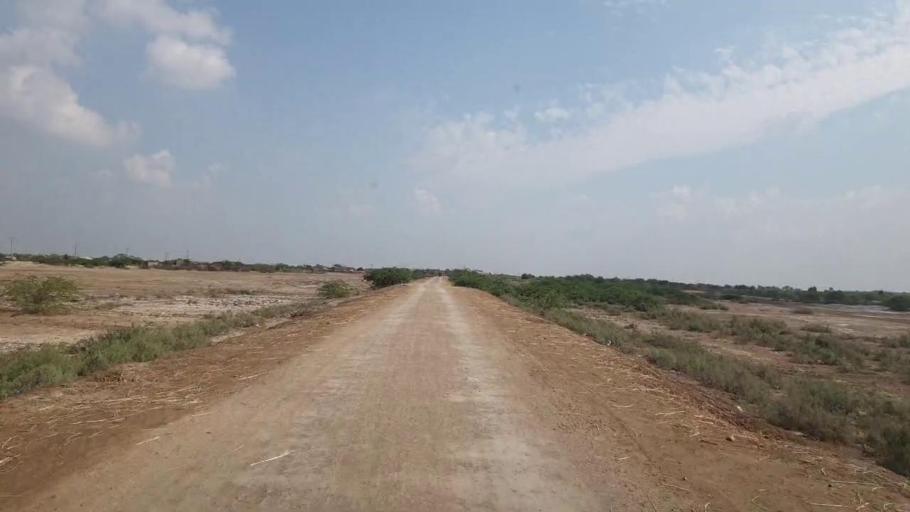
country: PK
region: Sindh
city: Badin
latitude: 24.4782
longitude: 68.6052
